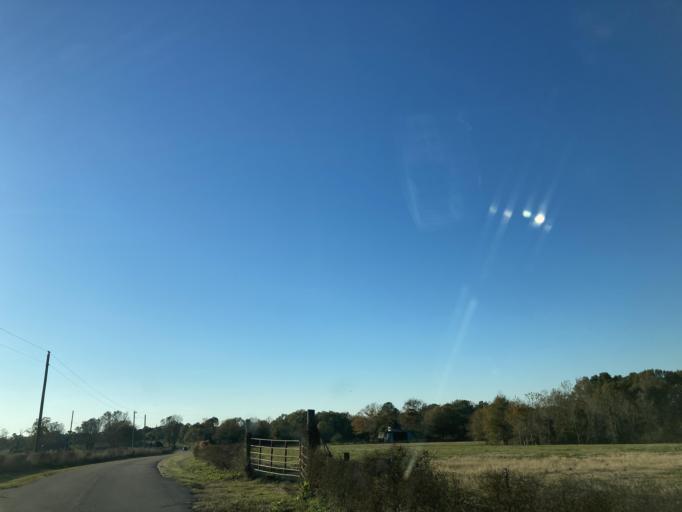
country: US
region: Mississippi
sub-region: Lamar County
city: Sumrall
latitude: 31.2678
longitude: -89.5932
